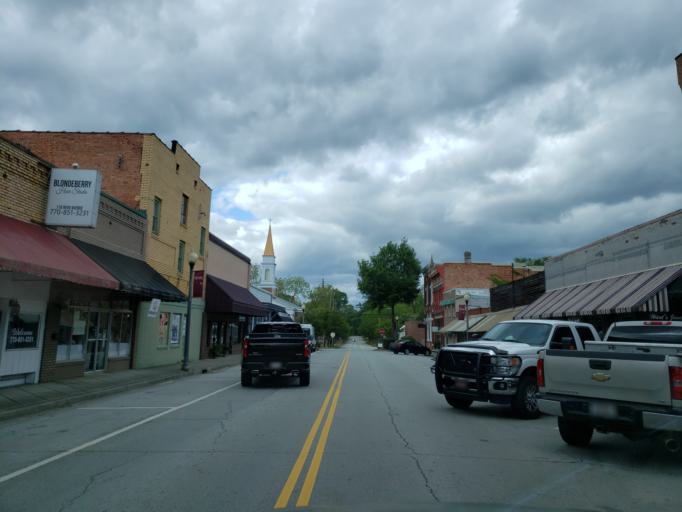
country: US
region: Georgia
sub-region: Haralson County
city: Tallapoosa
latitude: 33.7446
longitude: -85.2881
